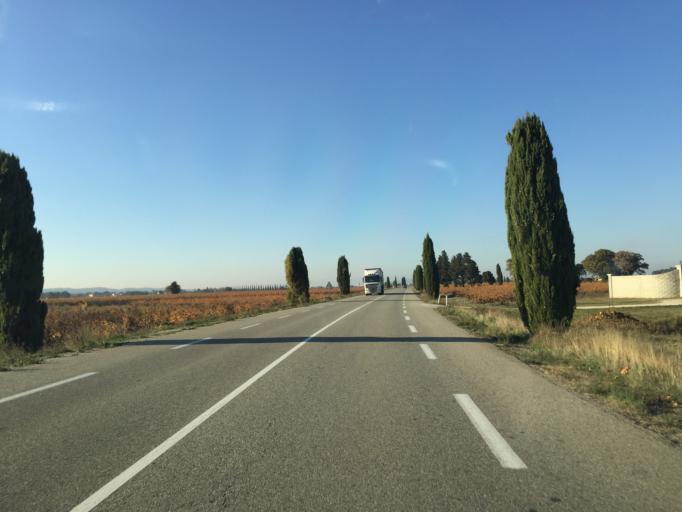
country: FR
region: Provence-Alpes-Cote d'Azur
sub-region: Departement du Vaucluse
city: Sainte-Cecile-les-Vignes
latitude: 44.2306
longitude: 4.9158
